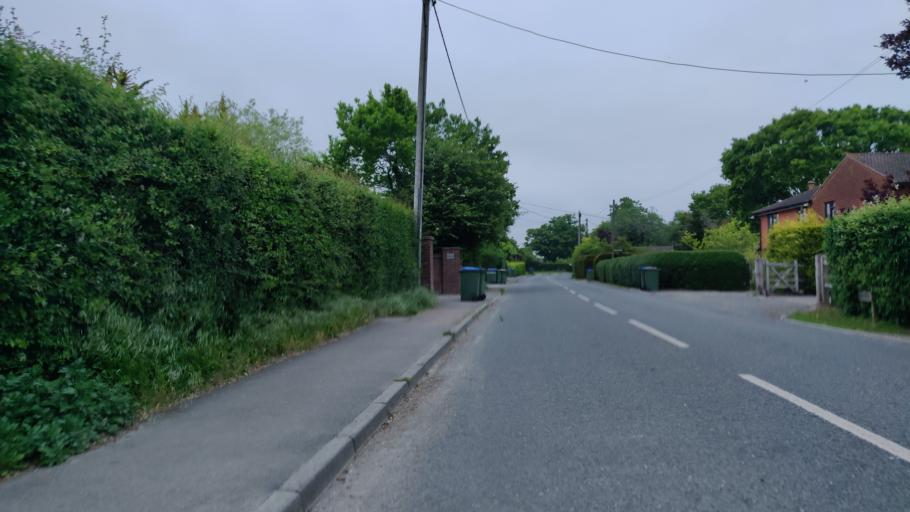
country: GB
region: England
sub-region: West Sussex
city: Partridge Green
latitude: 50.9687
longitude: -0.3039
